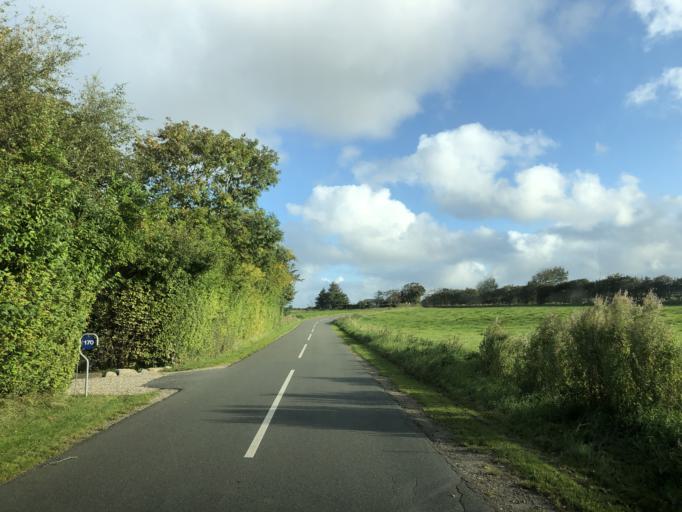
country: DK
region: Central Jutland
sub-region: Holstebro Kommune
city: Ulfborg
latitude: 56.3847
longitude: 8.3477
